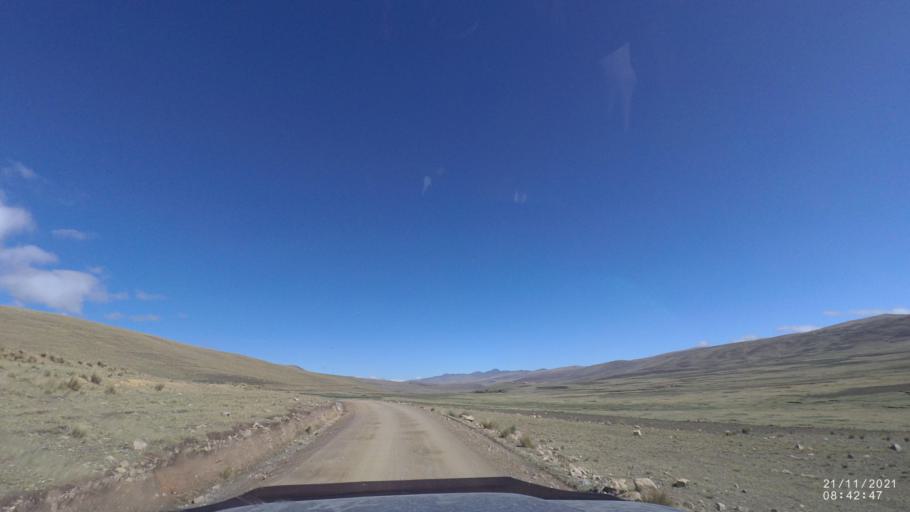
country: BO
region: Cochabamba
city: Cochabamba
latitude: -17.2644
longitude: -66.2220
